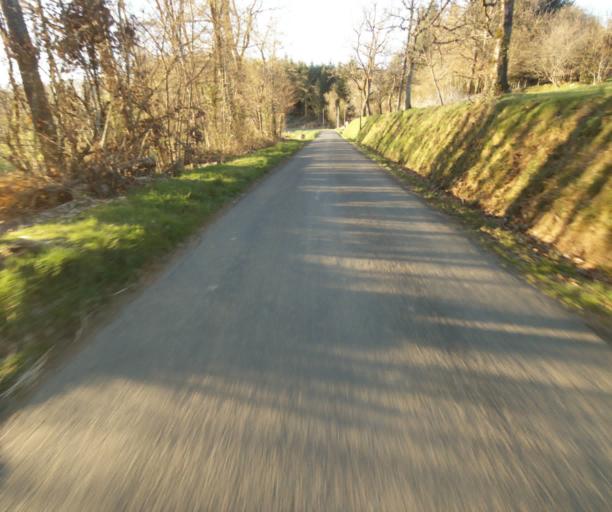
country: FR
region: Limousin
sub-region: Departement de la Correze
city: Saint-Clement
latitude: 45.3363
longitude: 1.7117
